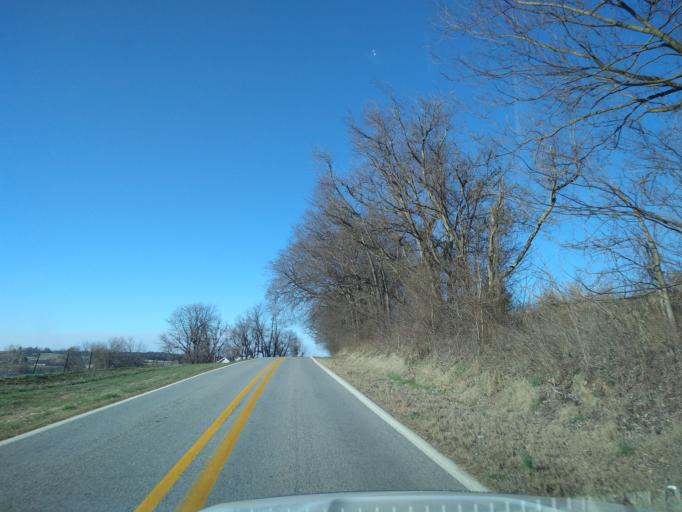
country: US
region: Arkansas
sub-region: Washington County
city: Lincoln
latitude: 35.9413
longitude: -94.3770
